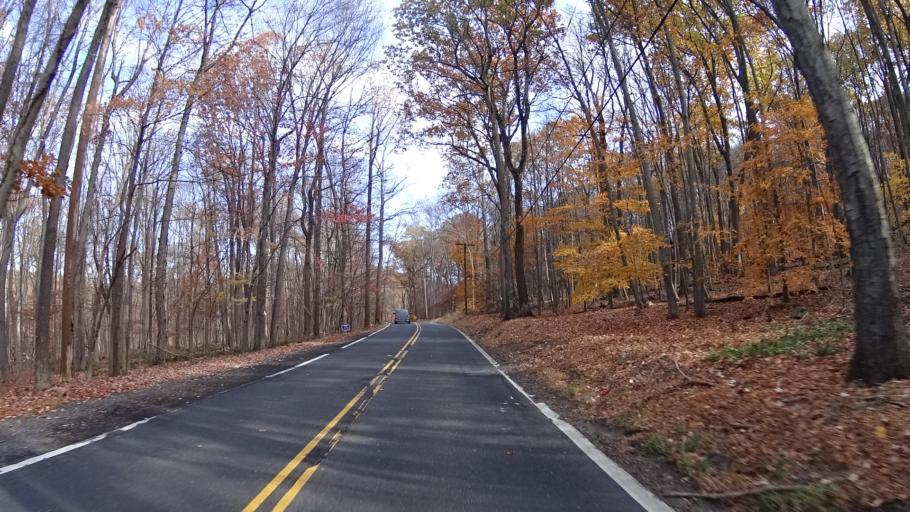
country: US
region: New Jersey
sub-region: Morris County
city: Mendham
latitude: 40.7670
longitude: -74.5594
